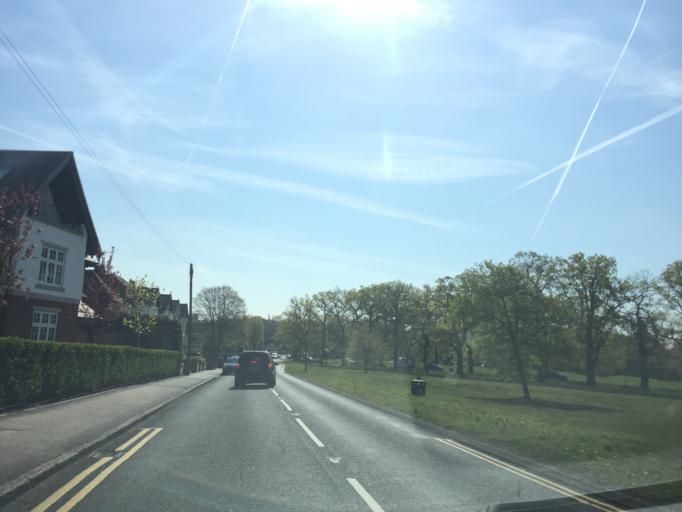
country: GB
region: England
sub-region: Essex
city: Theydon Bois
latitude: 51.6723
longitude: 0.0974
